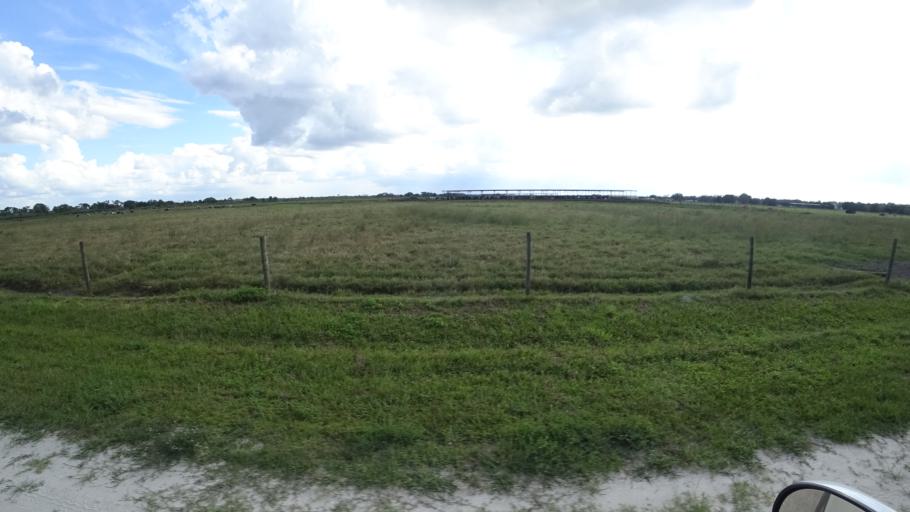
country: US
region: Florida
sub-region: DeSoto County
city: Arcadia
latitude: 27.2956
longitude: -82.1090
